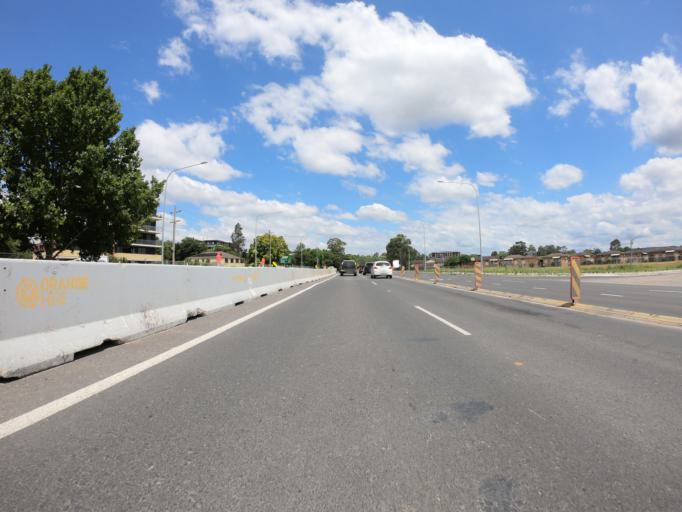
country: AU
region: New South Wales
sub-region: Penrith Municipality
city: Penrith
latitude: -33.7525
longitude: 150.6874
